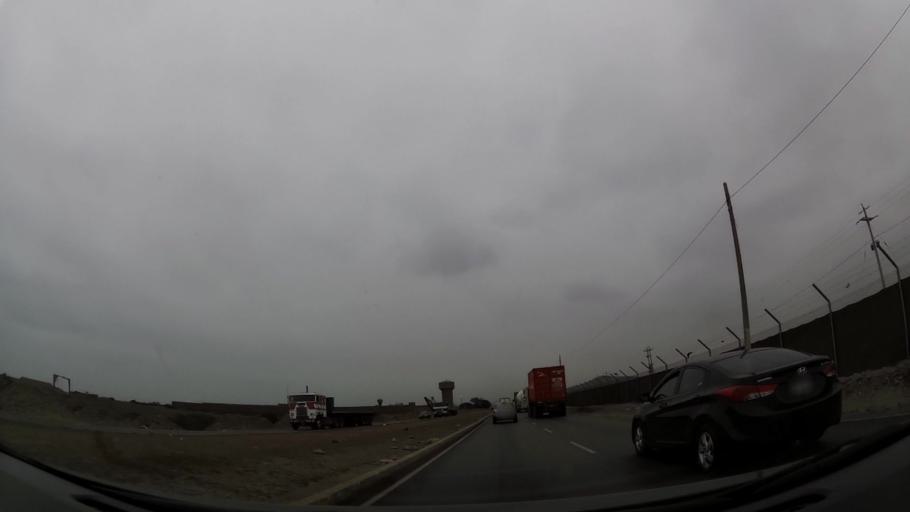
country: PE
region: Callao
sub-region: Callao
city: Callao
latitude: -12.0091
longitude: -77.1280
